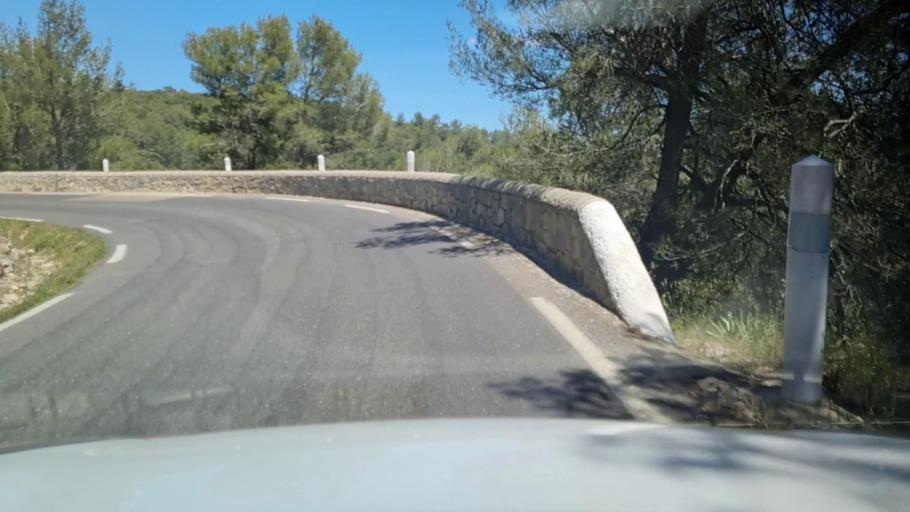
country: FR
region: Languedoc-Roussillon
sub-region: Departement du Gard
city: Clarensac
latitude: 43.8357
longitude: 4.2274
